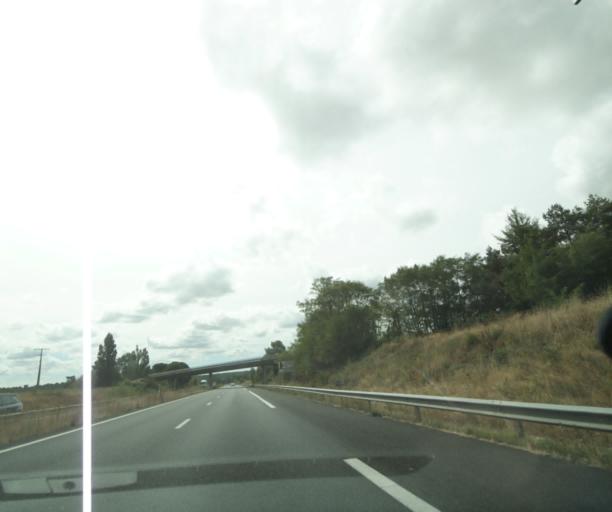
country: FR
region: Aquitaine
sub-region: Departement de la Gironde
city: Marcillac
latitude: 45.2762
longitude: -0.5506
